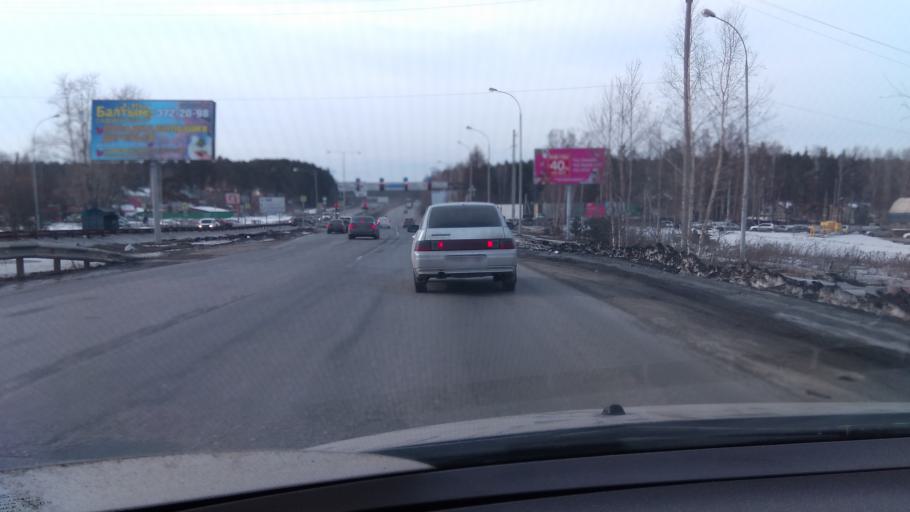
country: RU
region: Sverdlovsk
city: Shirokaya Rechka
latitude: 56.8210
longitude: 60.5023
